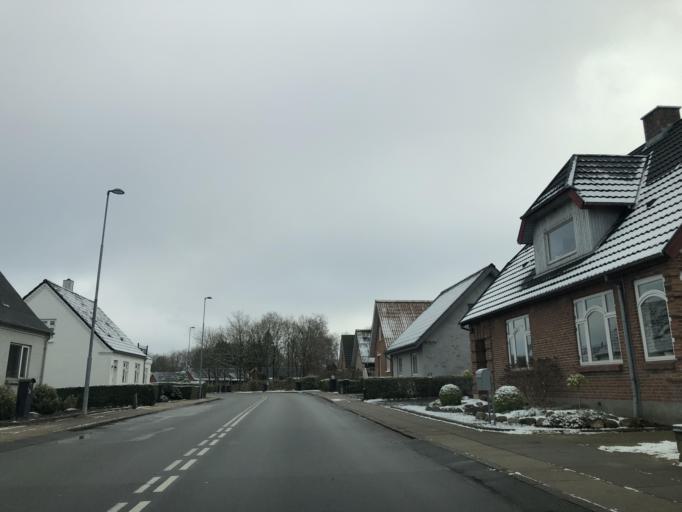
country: DK
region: South Denmark
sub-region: Vejle Kommune
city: Give
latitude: 55.9831
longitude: 9.2948
